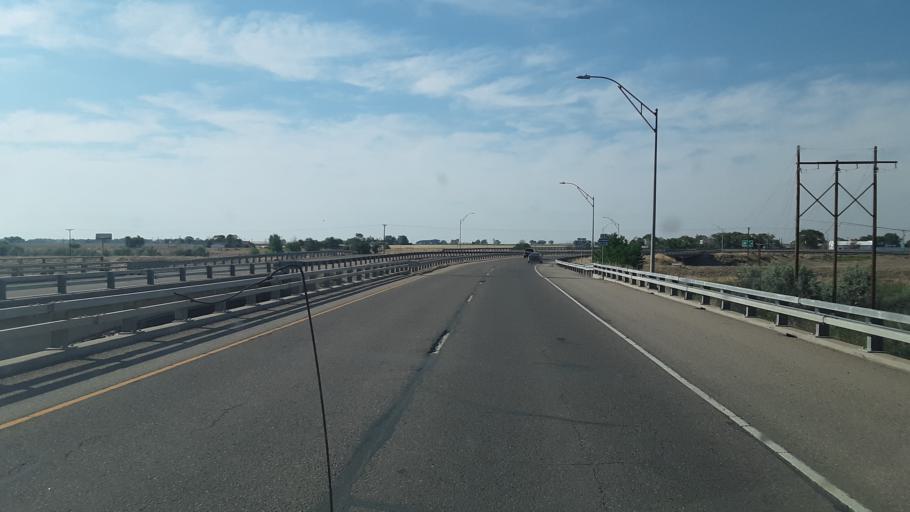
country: US
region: Colorado
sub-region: Bent County
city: Las Animas
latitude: 38.0826
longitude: -103.2201
